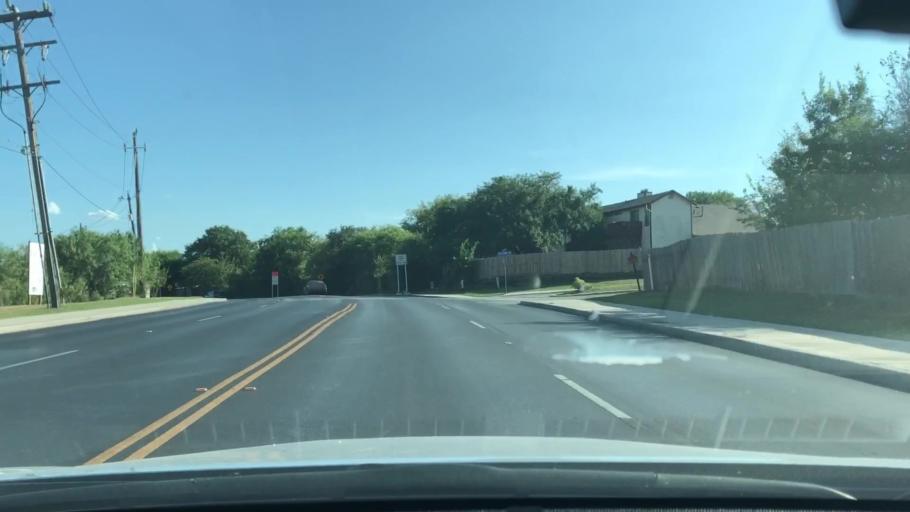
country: US
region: Texas
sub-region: Bexar County
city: Kirby
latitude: 29.4799
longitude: -98.3484
